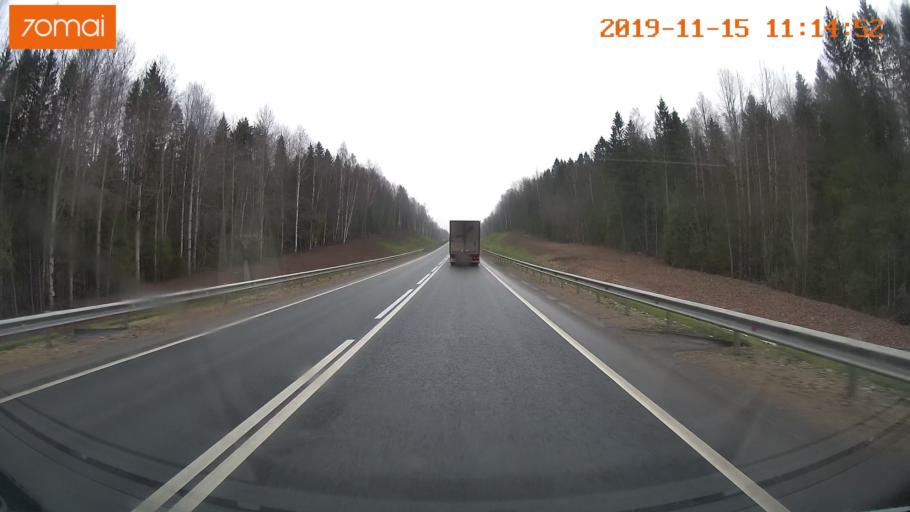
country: RU
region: Vologda
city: Chebsara
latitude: 59.1261
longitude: 39.1978
